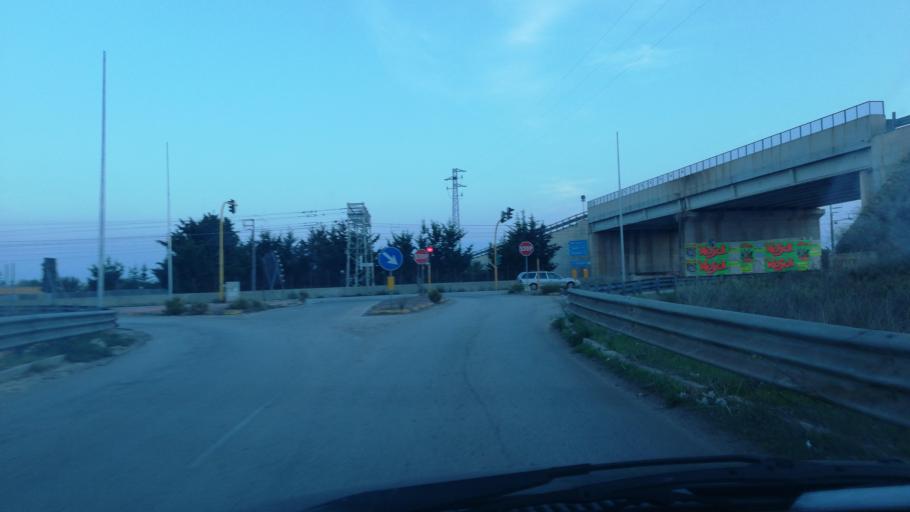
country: IT
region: Apulia
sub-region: Provincia di Bari
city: Bitonto
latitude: 41.1271
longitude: 16.7149
